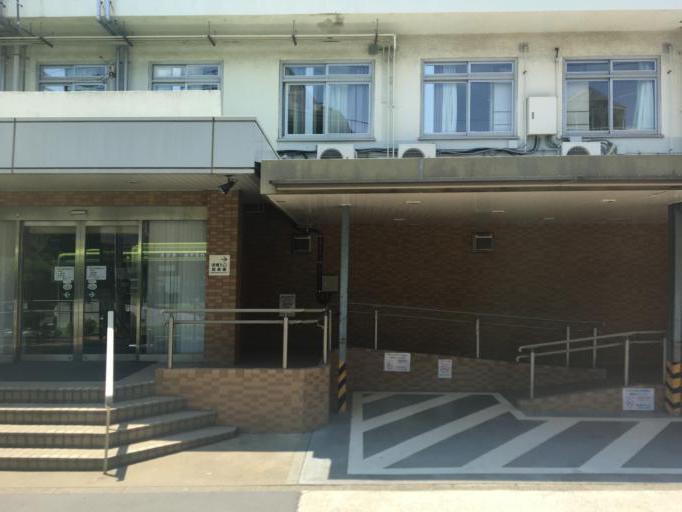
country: JP
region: Saitama
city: Kawaguchi
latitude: 35.7626
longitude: 139.6901
